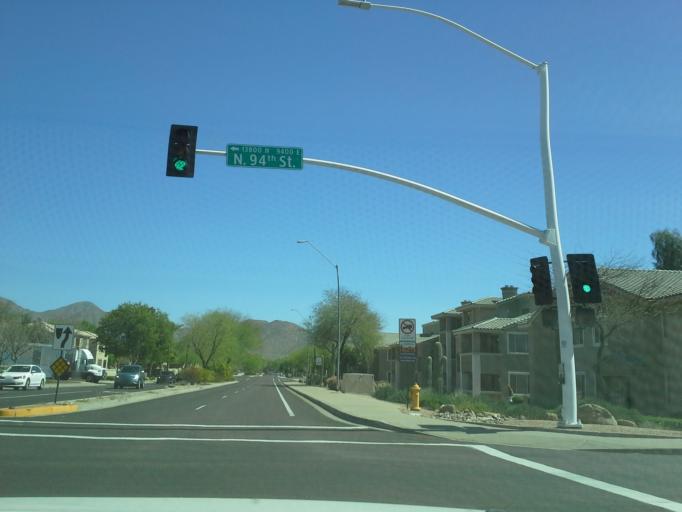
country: US
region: Arizona
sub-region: Maricopa County
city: Paradise Valley
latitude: 33.6115
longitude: -111.8784
